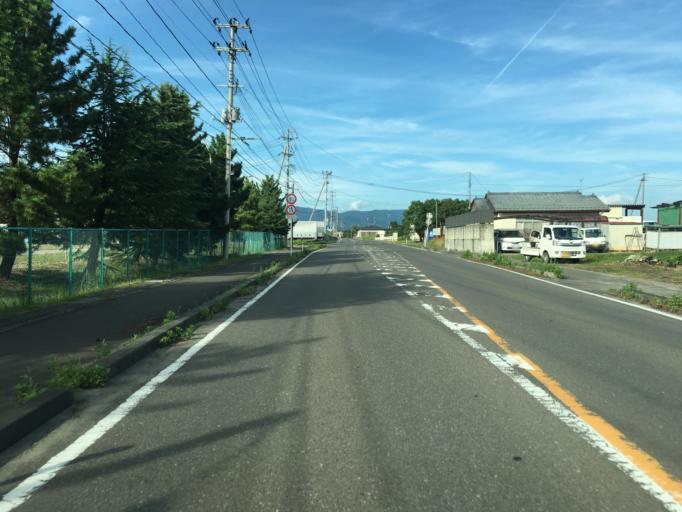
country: JP
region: Fukushima
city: Hobaramachi
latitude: 37.8324
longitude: 140.5072
